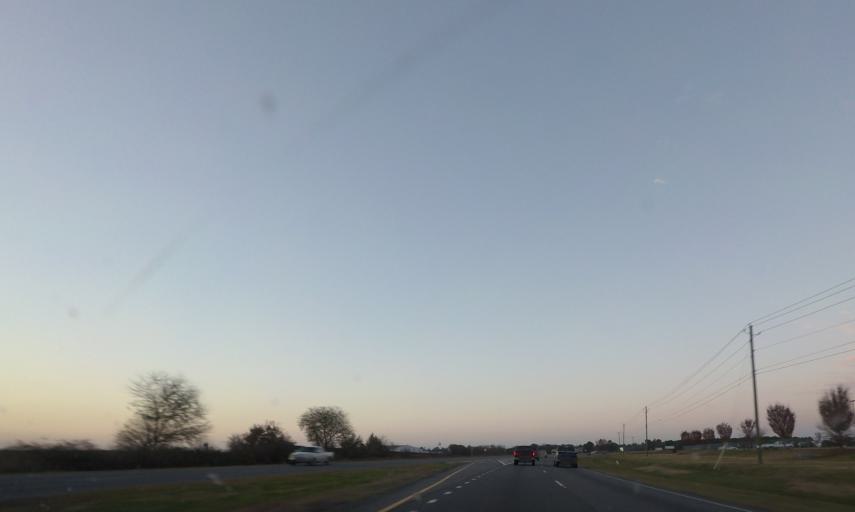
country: US
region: Georgia
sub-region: Houston County
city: Centerville
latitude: 32.6971
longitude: -83.6403
